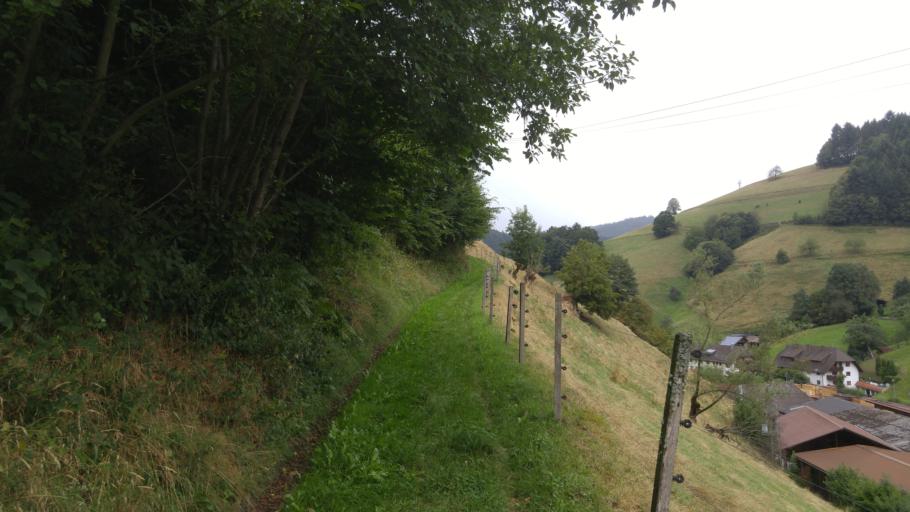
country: DE
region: Baden-Wuerttemberg
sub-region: Freiburg Region
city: Muenstertal/Schwarzwald
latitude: 47.8452
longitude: 7.7931
